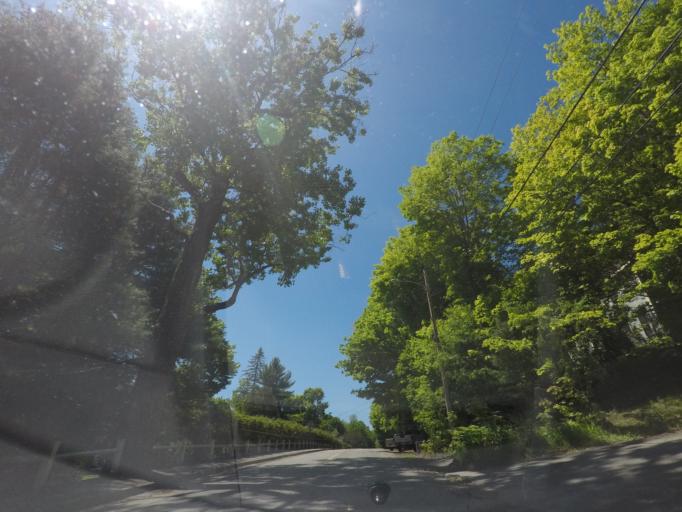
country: US
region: Maine
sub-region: Kennebec County
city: Hallowell
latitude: 44.2827
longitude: -69.7948
